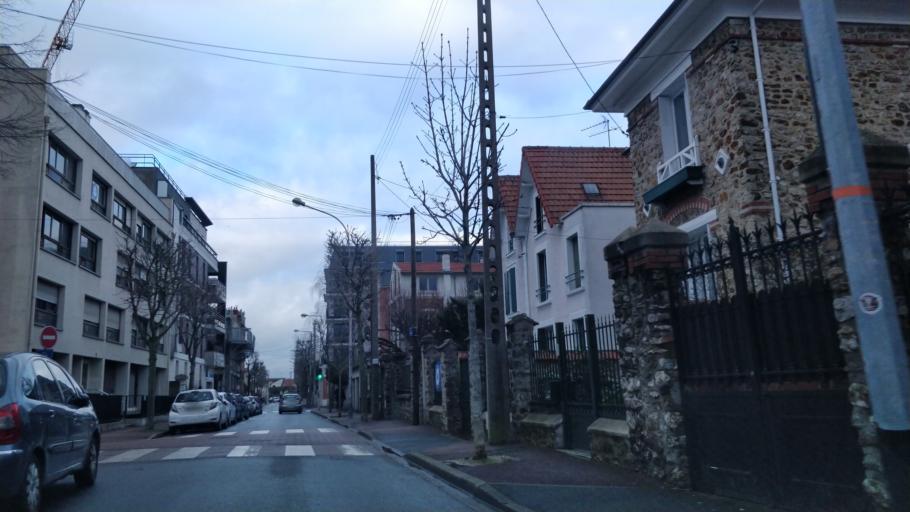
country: FR
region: Ile-de-France
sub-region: Departement de l'Essonne
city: Juvisy-sur-Orge
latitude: 48.6901
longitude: 2.3797
